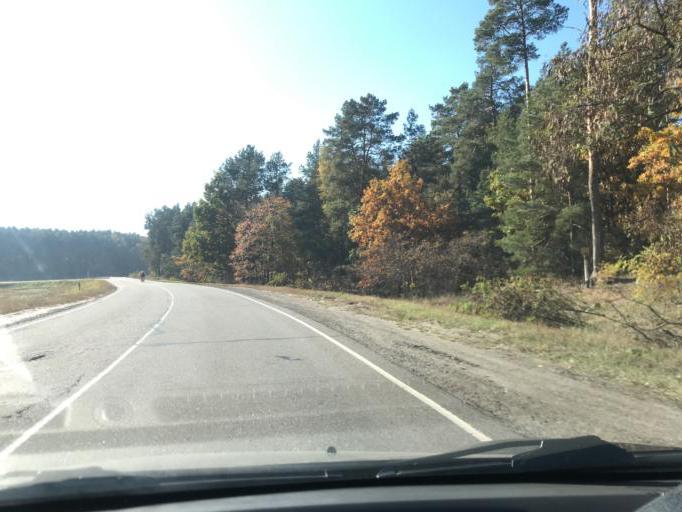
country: BY
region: Gomel
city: Gomel
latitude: 52.3893
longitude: 30.8258
